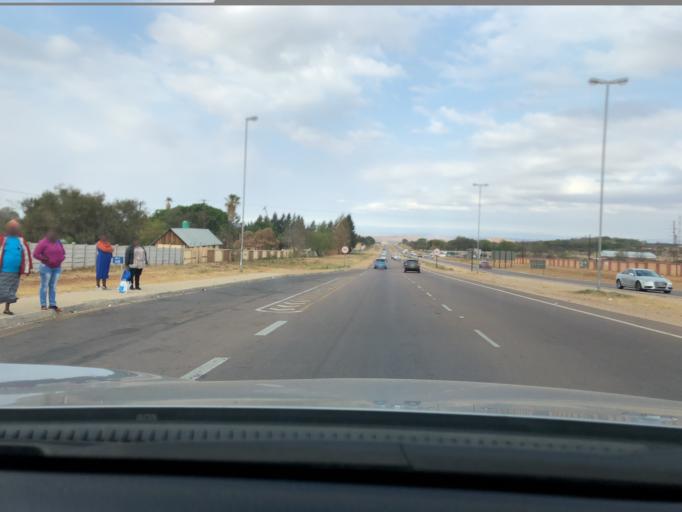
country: ZA
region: Limpopo
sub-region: Capricorn District Municipality
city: Polokwane
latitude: -23.8985
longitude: 29.5238
